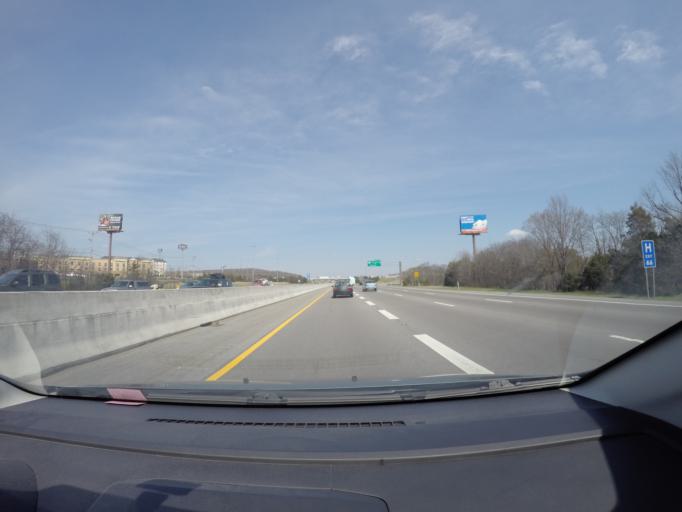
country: US
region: Tennessee
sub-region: Rutherford County
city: La Vergne
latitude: 35.9709
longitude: -86.5685
